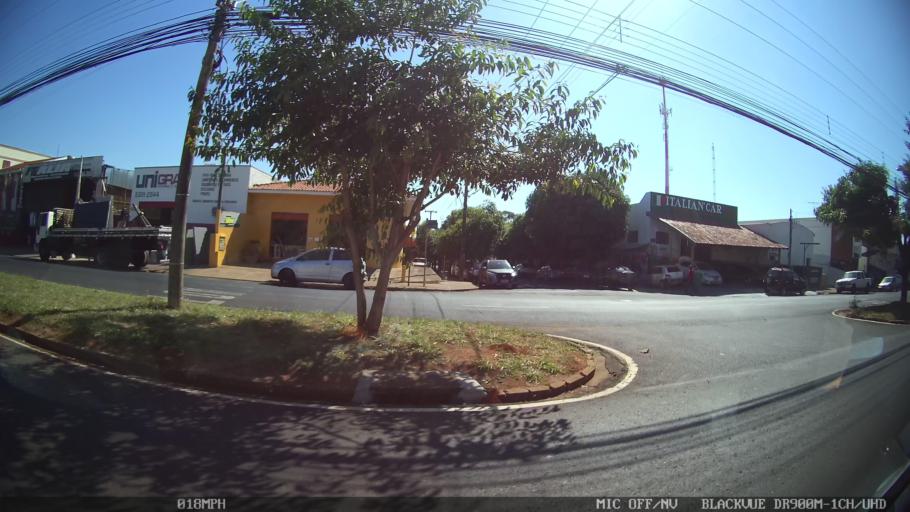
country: BR
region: Sao Paulo
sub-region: Sao Jose Do Rio Preto
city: Sao Jose do Rio Preto
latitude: -20.8096
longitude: -49.4078
